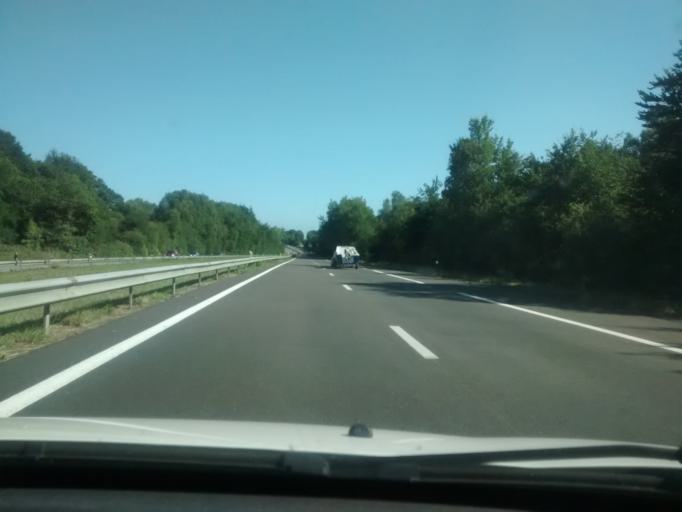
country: FR
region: Brittany
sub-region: Departement d'Ille-et-Vilaine
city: Miniac-Morvan
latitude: 48.4858
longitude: -1.9076
